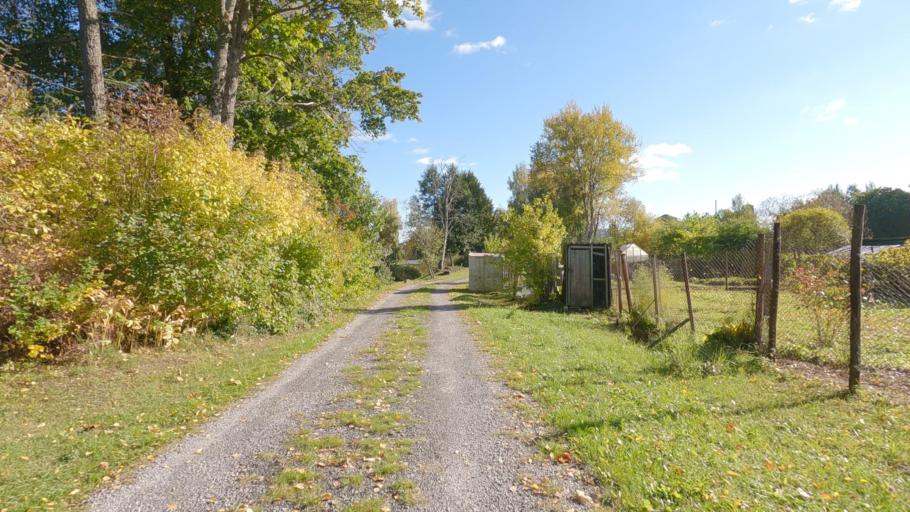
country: EE
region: Raplamaa
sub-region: Rapla vald
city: Rapla
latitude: 58.9959
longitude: 24.8312
